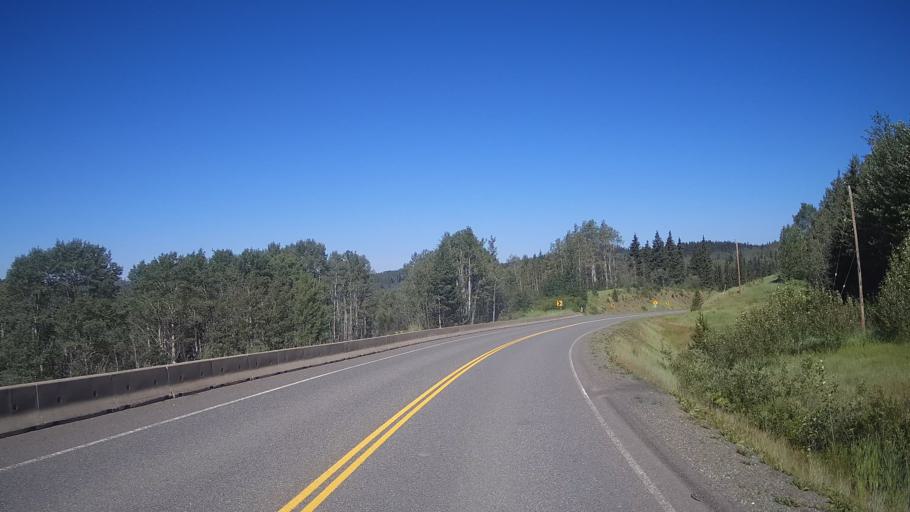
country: CA
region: British Columbia
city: Kamloops
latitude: 51.4993
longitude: -120.5965
